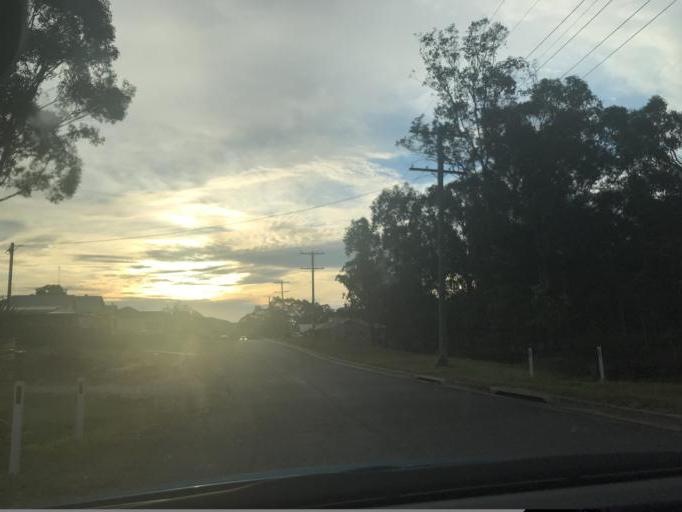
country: AU
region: New South Wales
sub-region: Cessnock
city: Cessnock
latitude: -32.9022
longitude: 151.2900
